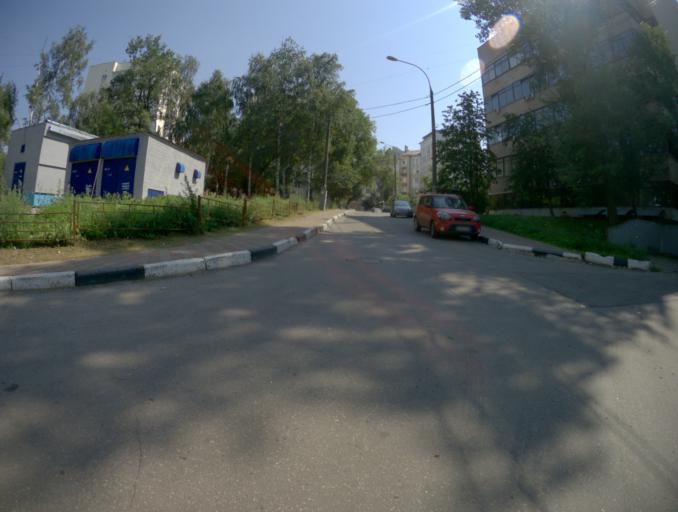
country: RU
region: Nizjnij Novgorod
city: Nizhniy Novgorod
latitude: 56.3234
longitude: 43.9845
